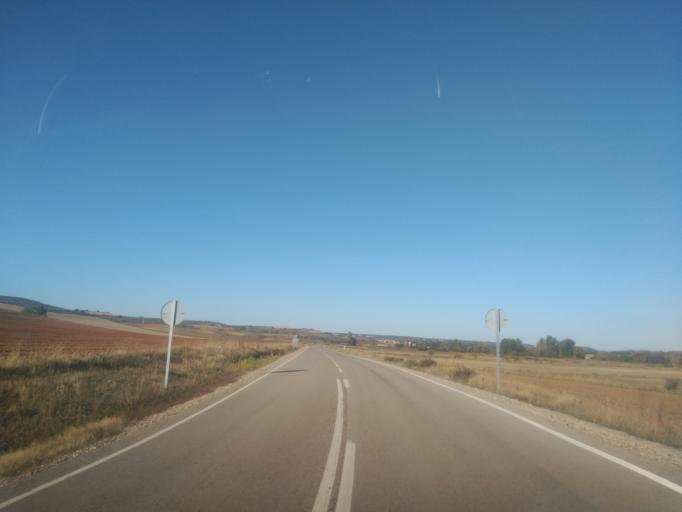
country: ES
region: Castille and Leon
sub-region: Provincia de Soria
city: Espeja de San Marcelino
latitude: 41.7573
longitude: -3.2449
